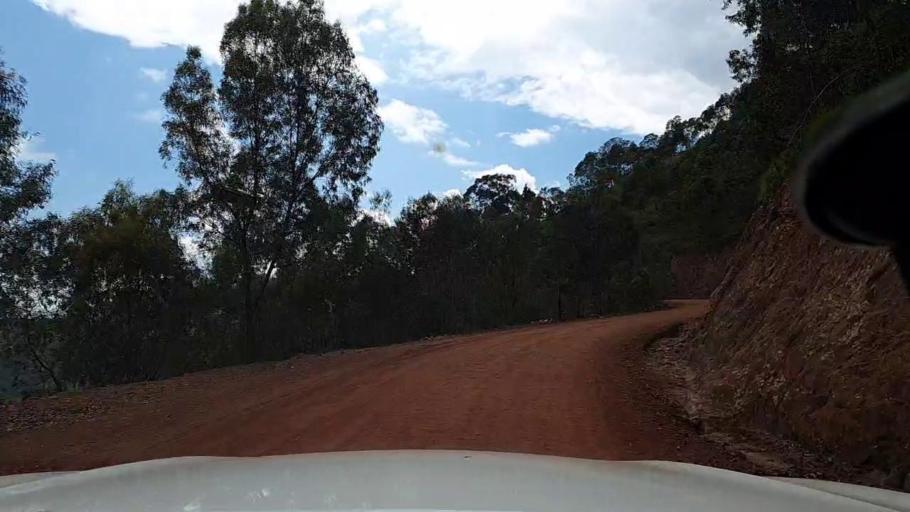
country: RW
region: Kigali
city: Kigali
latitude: -1.7584
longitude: 29.8458
